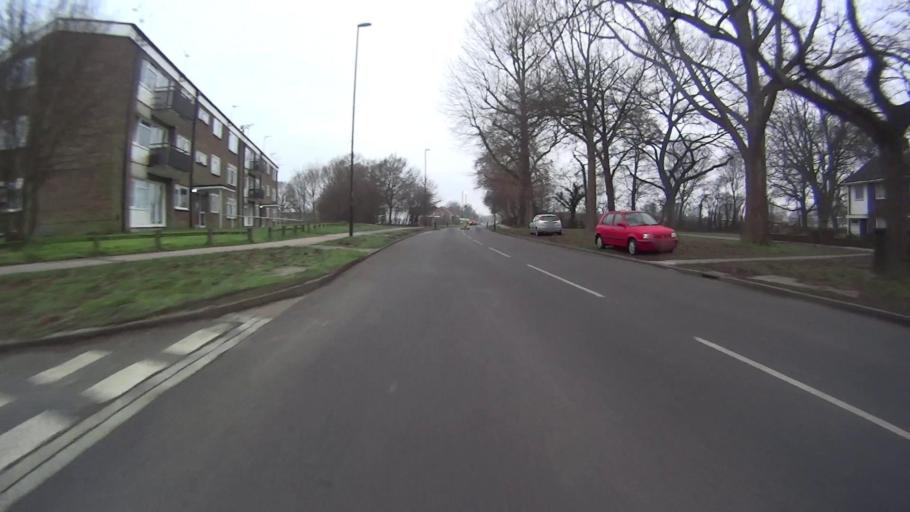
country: GB
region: England
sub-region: West Sussex
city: Furnace Green
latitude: 51.1026
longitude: -0.1732
